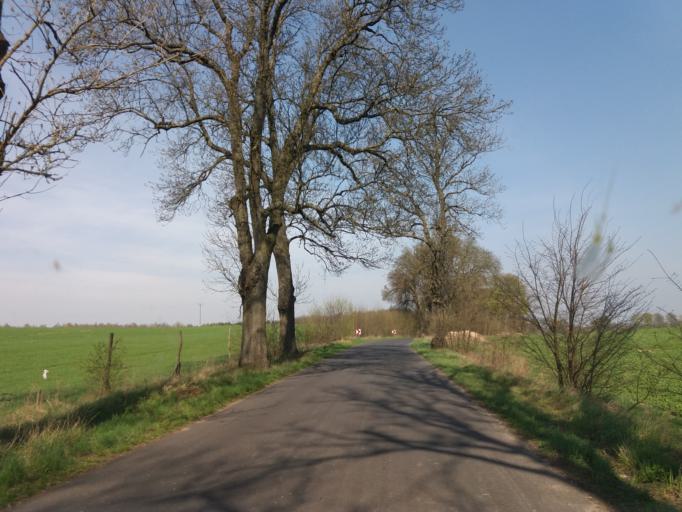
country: PL
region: West Pomeranian Voivodeship
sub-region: Powiat choszczenski
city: Recz
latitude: 53.2413
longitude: 15.6056
